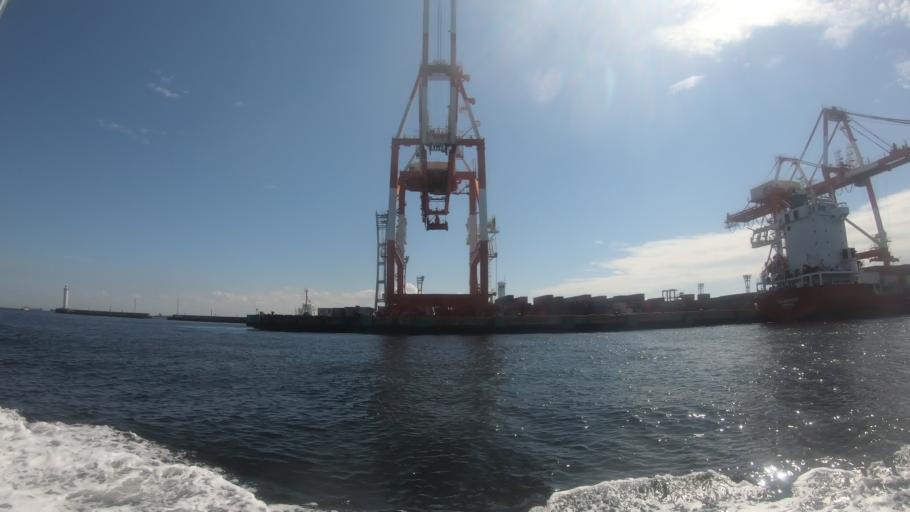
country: JP
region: Kanagawa
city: Yokohama
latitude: 35.4421
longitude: 139.6841
